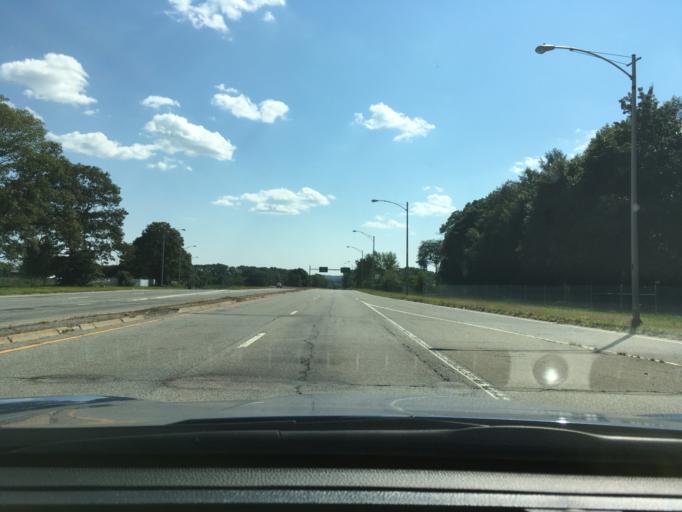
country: US
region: Rhode Island
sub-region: Providence County
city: Cranston
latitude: 41.7454
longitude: -71.4709
